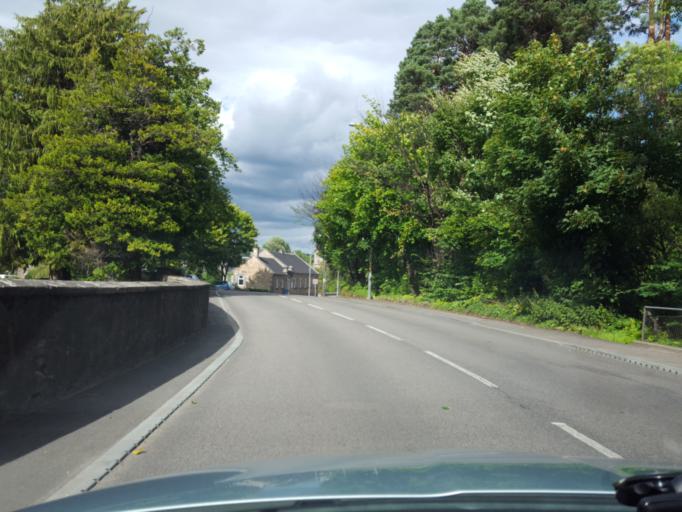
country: GB
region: Scotland
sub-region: Moray
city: Rothes
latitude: 57.4685
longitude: -3.2288
